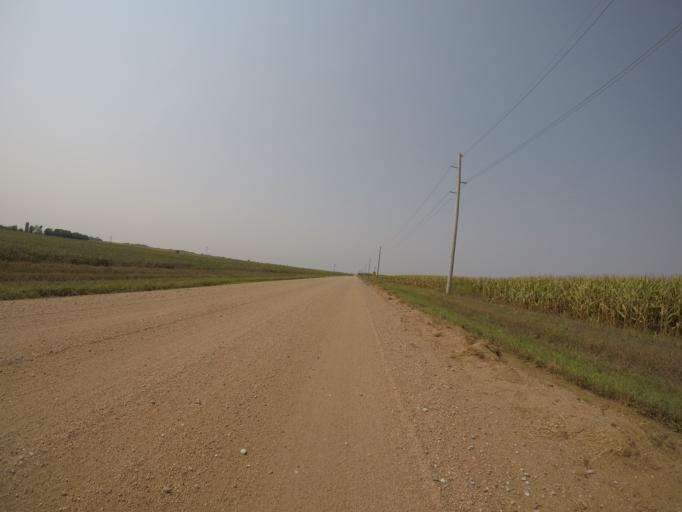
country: US
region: Nebraska
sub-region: Gage County
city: Beatrice
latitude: 40.2774
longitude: -96.8200
